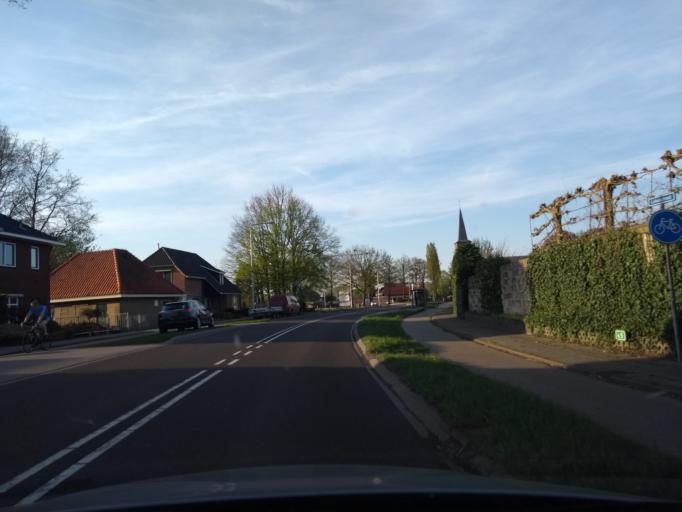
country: NL
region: Overijssel
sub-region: Gemeente Almelo
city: Almelo
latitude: 52.3071
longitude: 6.6548
